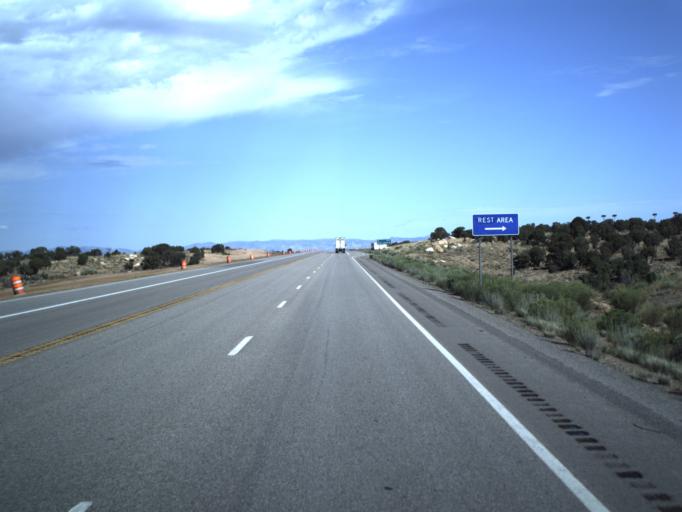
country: US
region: Utah
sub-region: Carbon County
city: East Carbon City
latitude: 39.4082
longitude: -110.4298
